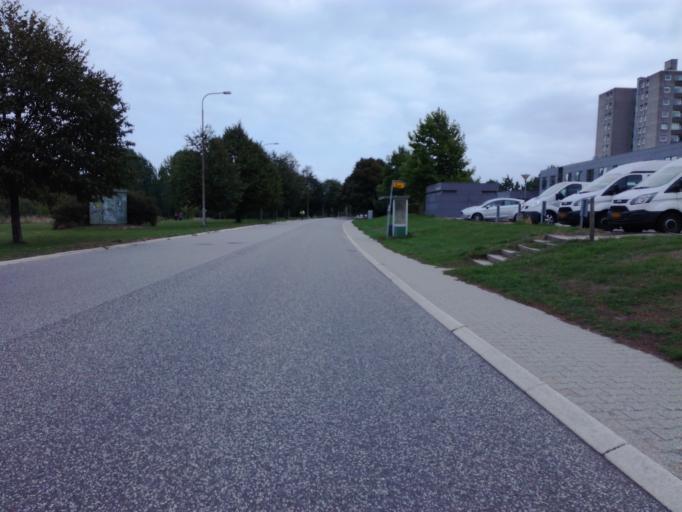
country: DK
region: South Denmark
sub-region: Fredericia Kommune
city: Fredericia
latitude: 55.5726
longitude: 9.7309
